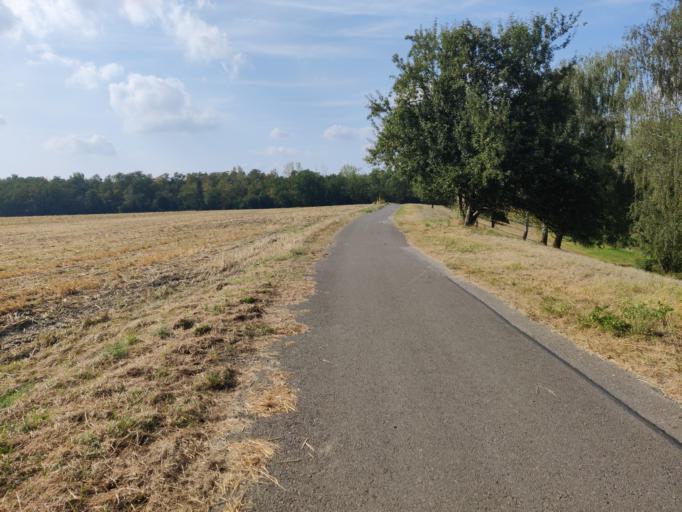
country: DE
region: Saxony
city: Regis-Breitingen
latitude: 51.0956
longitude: 12.4342
